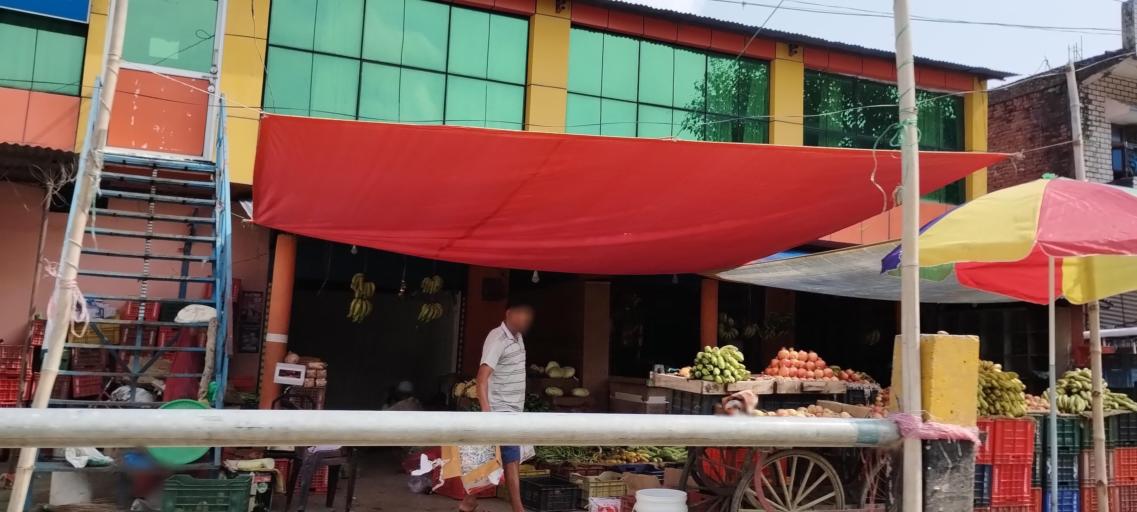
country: NP
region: Mid Western
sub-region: Bheri Zone
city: Nepalgunj
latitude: 28.0990
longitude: 81.6657
